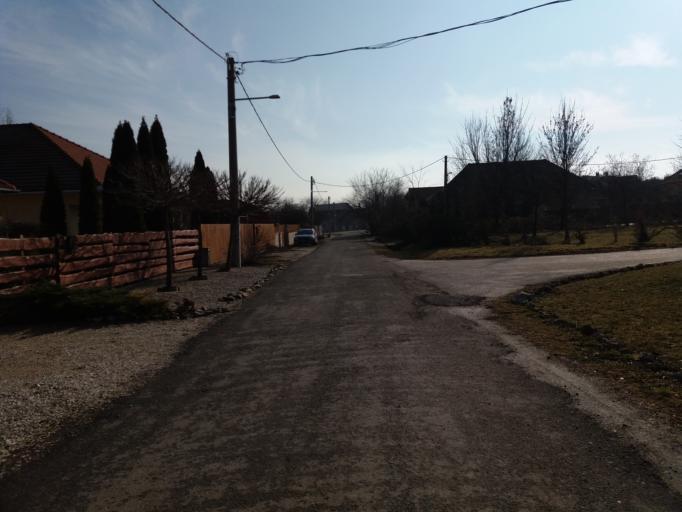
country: HU
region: Pest
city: Paty
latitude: 47.5160
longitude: 18.8116
